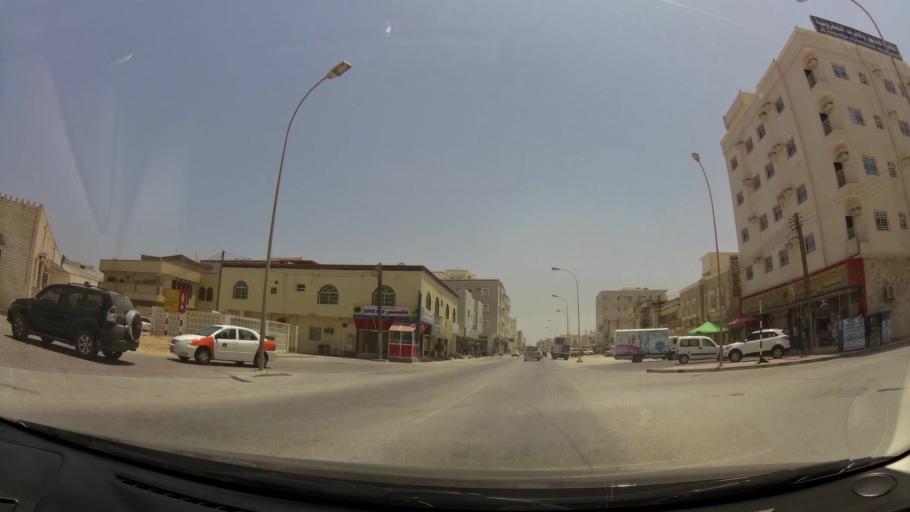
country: OM
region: Zufar
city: Salalah
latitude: 17.0174
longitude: 54.0831
